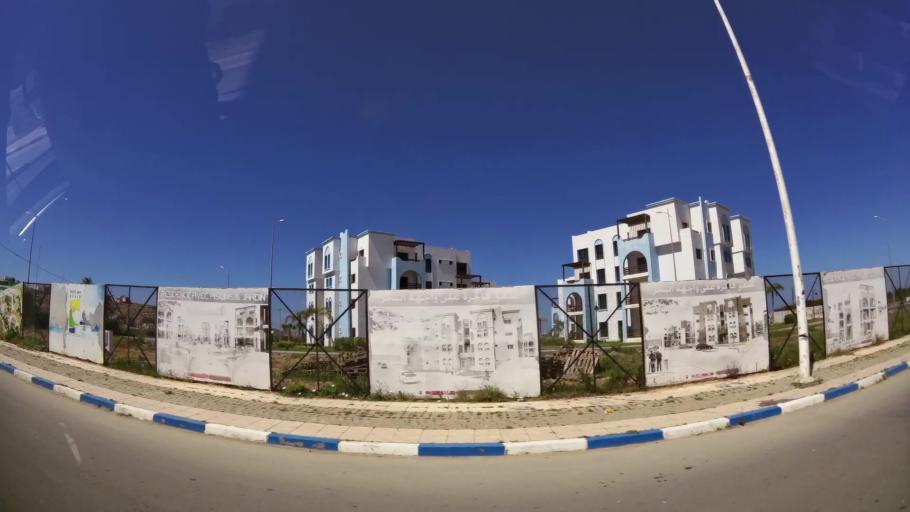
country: MA
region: Oriental
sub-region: Berkane-Taourirt
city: Madagh
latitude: 35.1385
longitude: -2.4211
